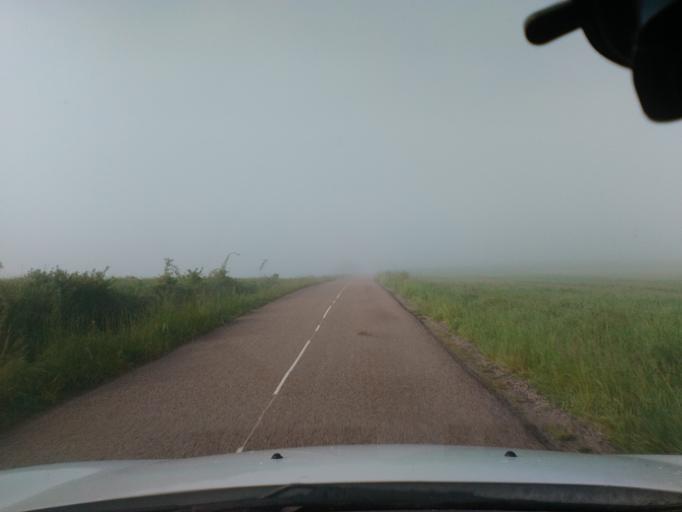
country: FR
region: Lorraine
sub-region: Departement des Vosges
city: Charmes
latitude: 48.3459
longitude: 6.2387
